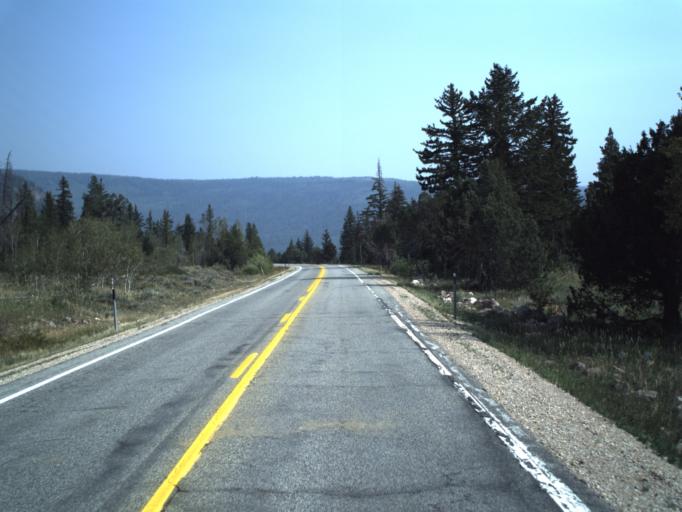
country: US
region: Utah
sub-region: Summit County
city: Francis
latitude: 40.5888
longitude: -111.0653
